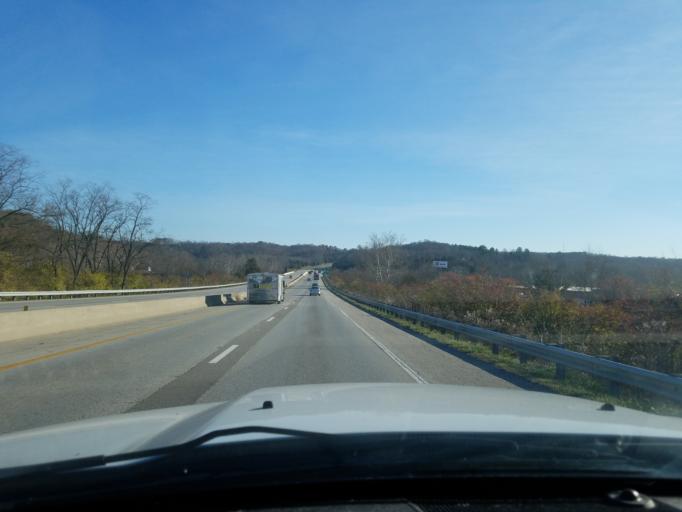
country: US
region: Ohio
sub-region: Clermont County
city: Batavia
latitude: 39.0847
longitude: -84.1841
